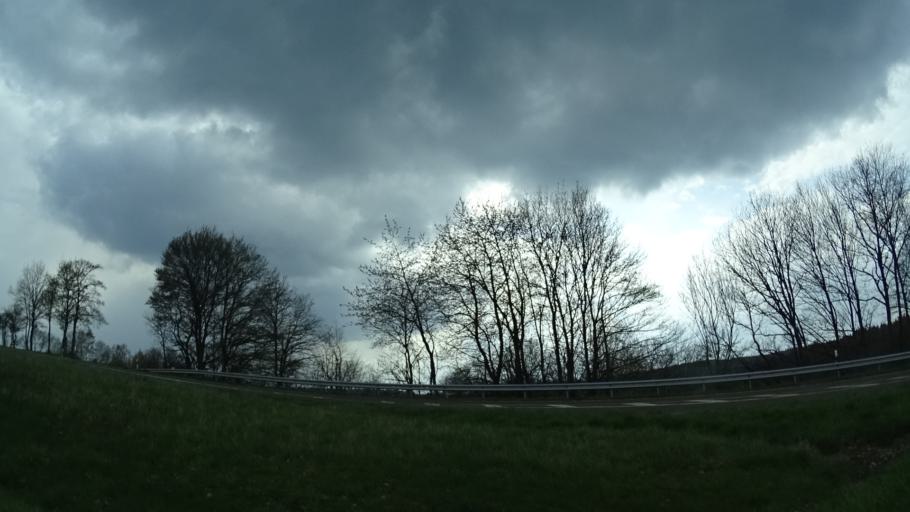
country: DE
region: Rheinland-Pfalz
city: Langenthal
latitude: 49.8537
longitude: 7.5797
